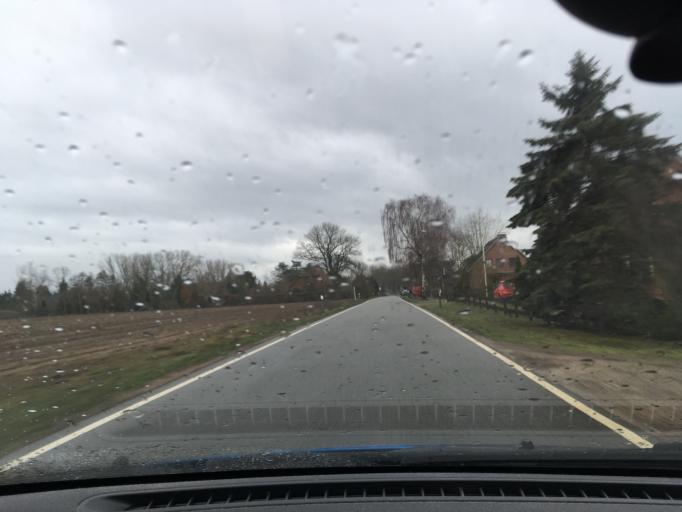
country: DE
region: Lower Saxony
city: Hittbergen
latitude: 53.3498
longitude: 10.5981
